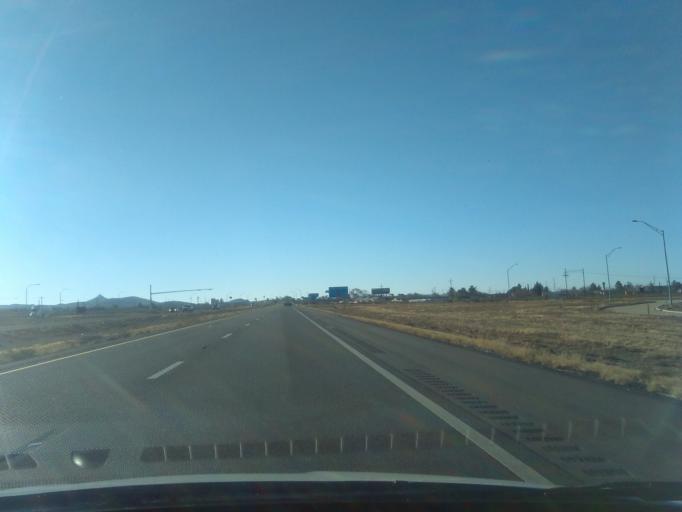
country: US
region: New Mexico
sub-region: Hidalgo County
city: Lordsburg
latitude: 32.3414
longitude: -108.6974
